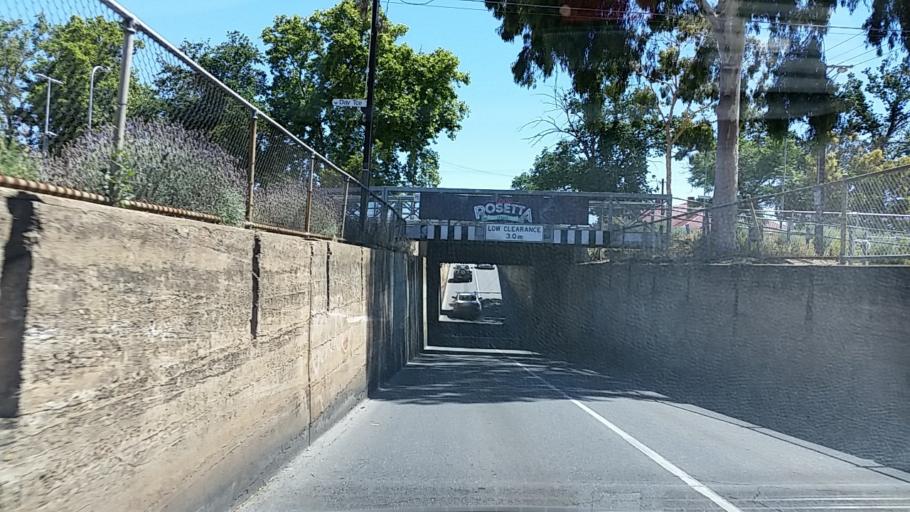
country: AU
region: South Australia
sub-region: Charles Sturt
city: Allenby Gardens
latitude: -34.8912
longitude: 138.5569
